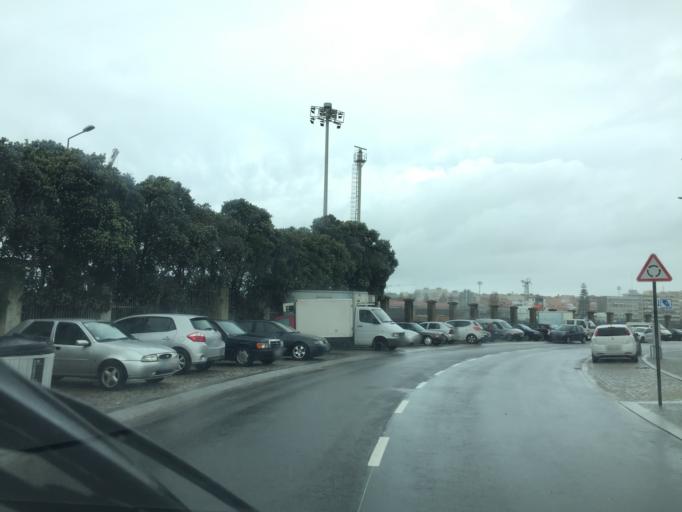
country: PT
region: Porto
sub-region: Matosinhos
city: Leca da Palmeira
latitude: 41.1847
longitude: -8.6965
